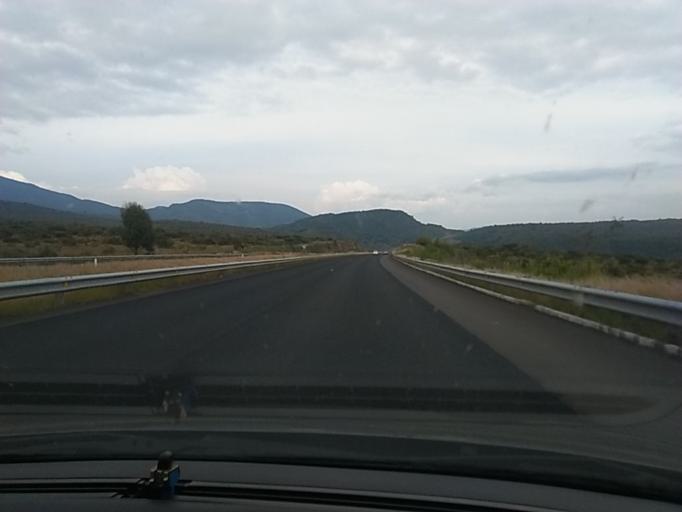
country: MX
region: Mexico
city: Huaniqueo de Morales
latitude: 19.8865
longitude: -101.4770
